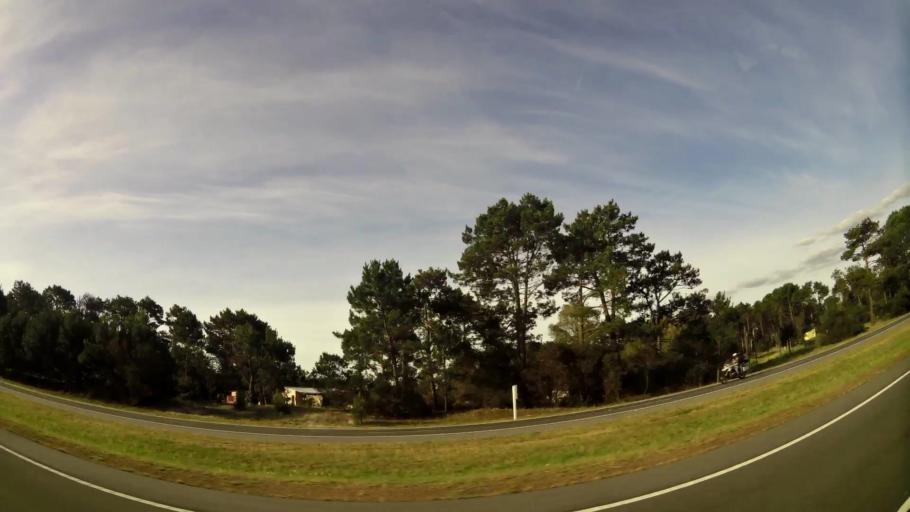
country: UY
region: Maldonado
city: Piriapolis
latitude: -34.7811
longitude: -55.4099
